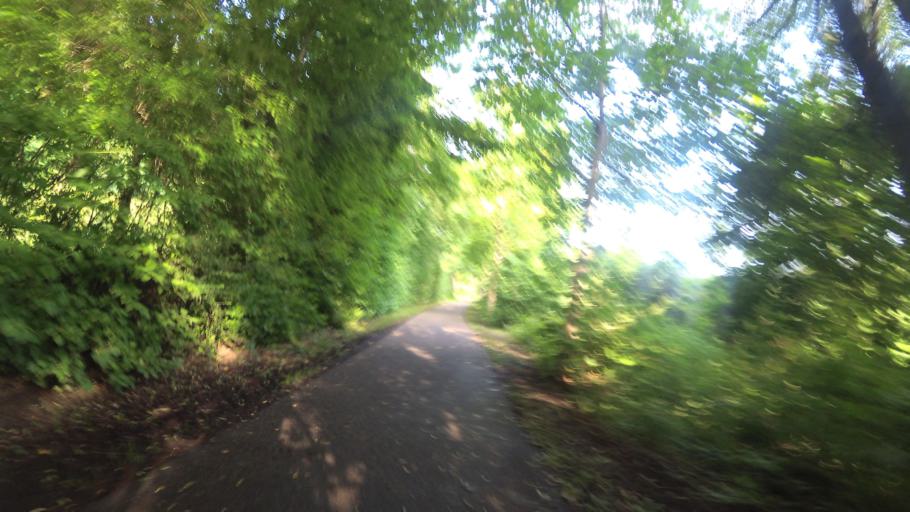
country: DE
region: Rheinland-Pfalz
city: Zweibrucken
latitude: 49.2255
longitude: 7.3728
